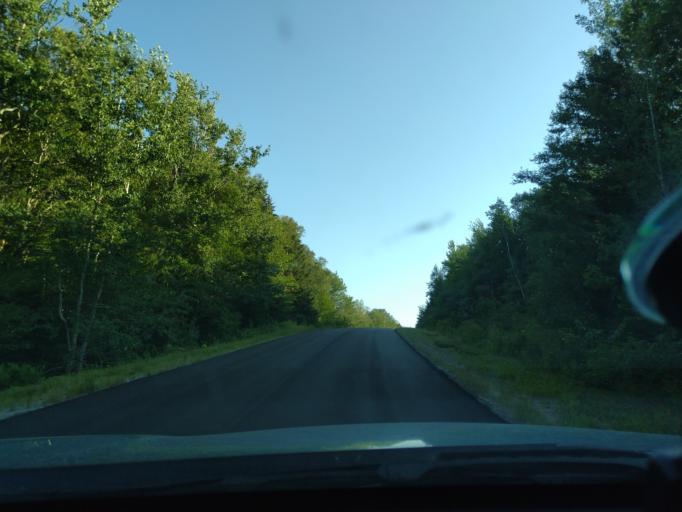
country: US
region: Maine
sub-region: Washington County
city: Eastport
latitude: 44.7148
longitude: -67.1384
